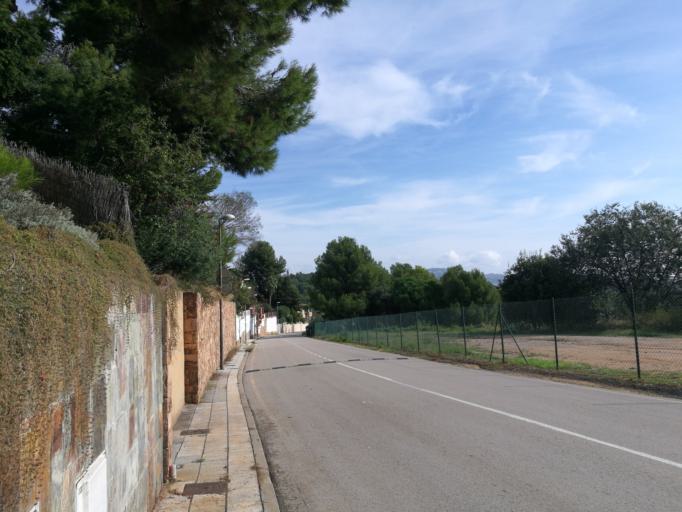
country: ES
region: Catalonia
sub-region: Provincia de Girona
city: Blanes
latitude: 41.6865
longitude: 2.8112
